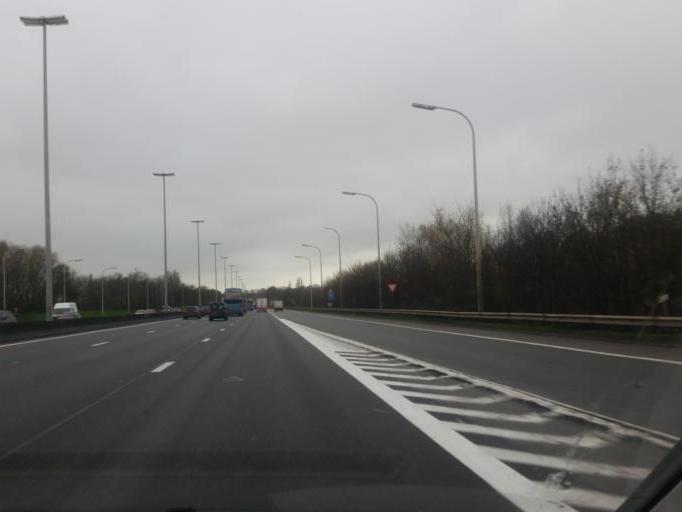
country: BE
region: Flanders
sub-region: Provincie Vlaams-Brabant
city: Grimbergen
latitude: 50.9137
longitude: 4.3866
